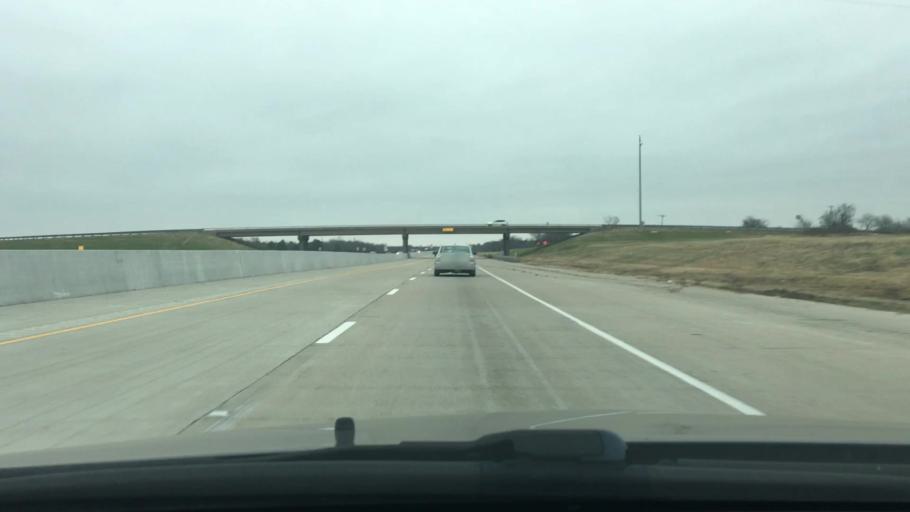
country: US
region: Texas
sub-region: Freestone County
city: Wortham
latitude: 31.8801
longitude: -96.3458
